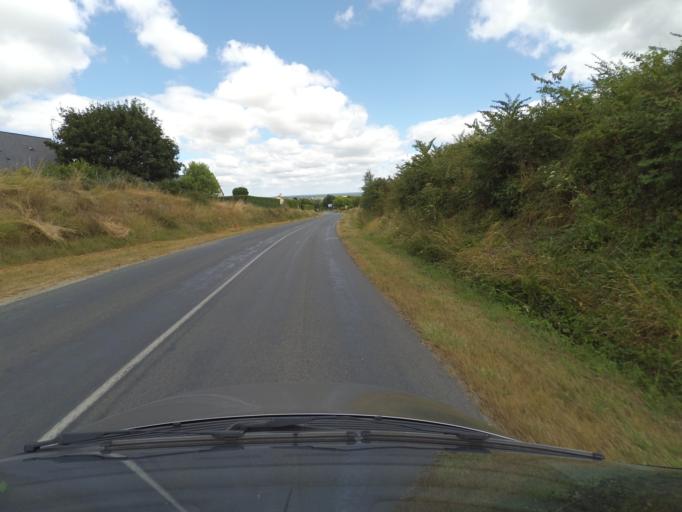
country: FR
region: Pays de la Loire
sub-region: Departement de Maine-et-Loire
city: Gennes
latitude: 47.3327
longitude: -0.2351
